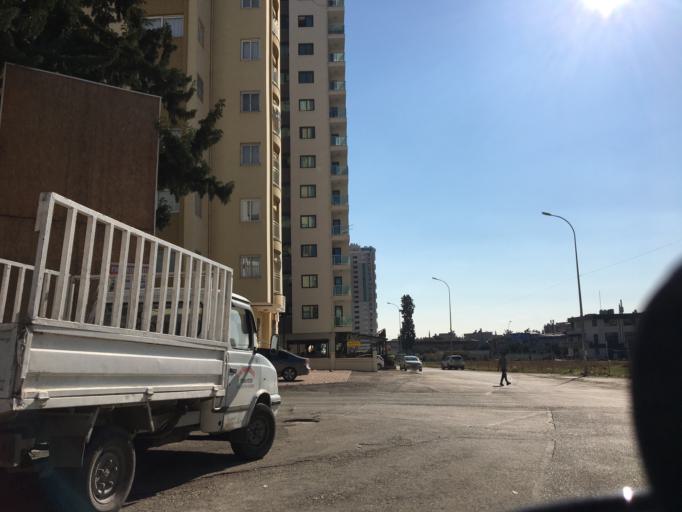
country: TR
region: Adana
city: Seyhan
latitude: 37.0201
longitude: 35.2849
